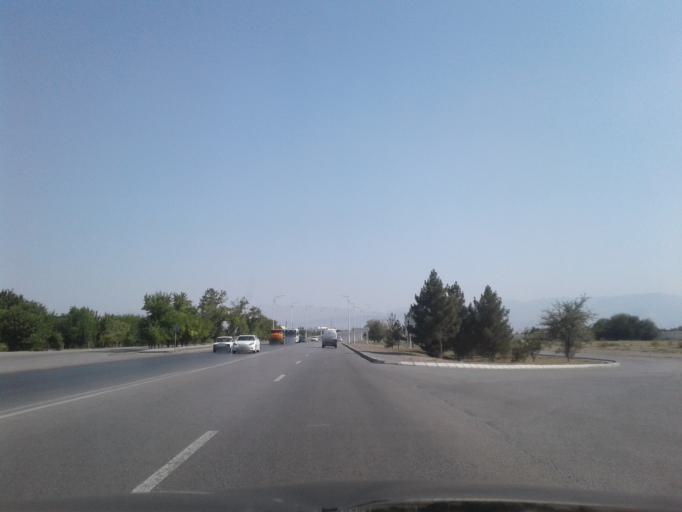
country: TM
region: Ahal
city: Ashgabat
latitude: 37.9687
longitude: 58.4225
